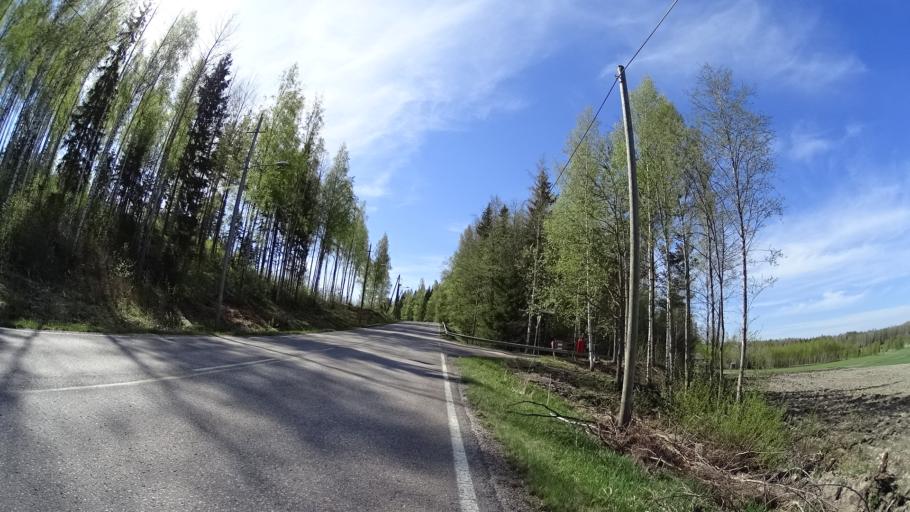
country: FI
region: Uusimaa
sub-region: Helsinki
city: Nurmijaervi
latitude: 60.3734
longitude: 24.8375
